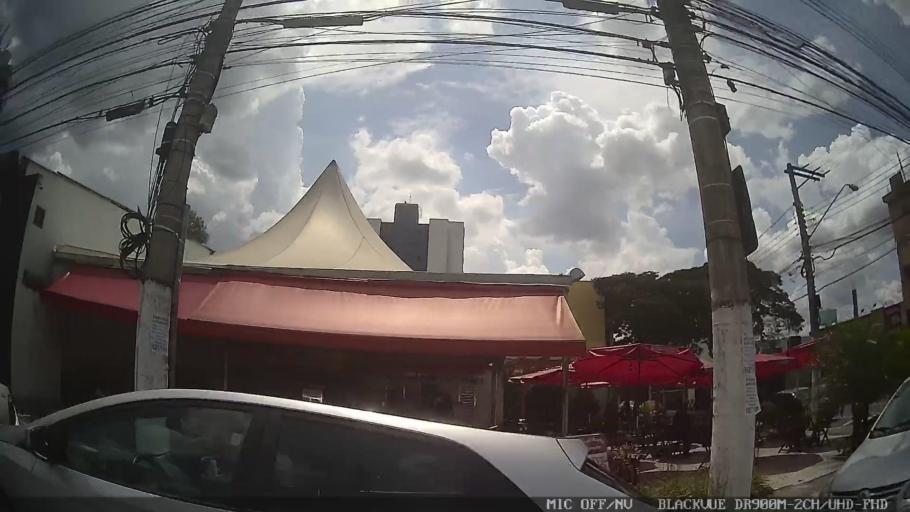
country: BR
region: Sao Paulo
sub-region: Suzano
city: Suzano
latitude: -23.5425
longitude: -46.3125
